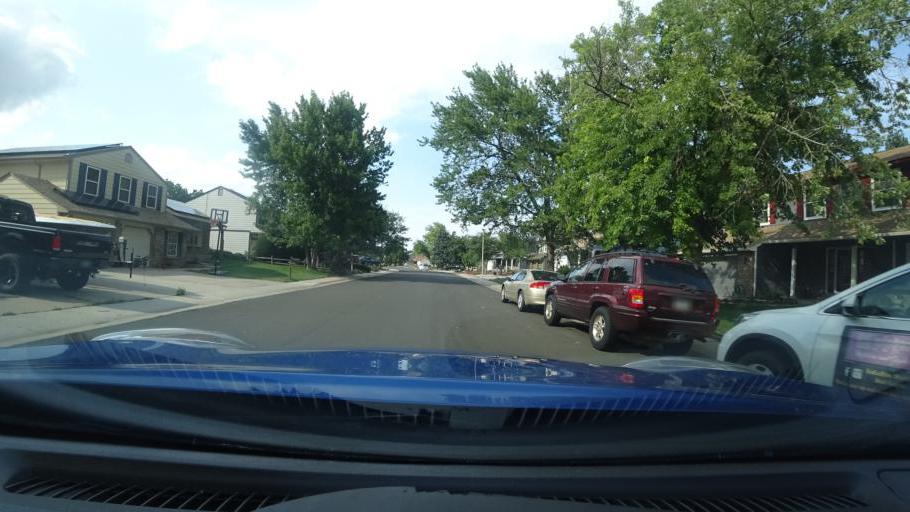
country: US
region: Colorado
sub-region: Adams County
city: Aurora
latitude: 39.6945
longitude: -104.8022
